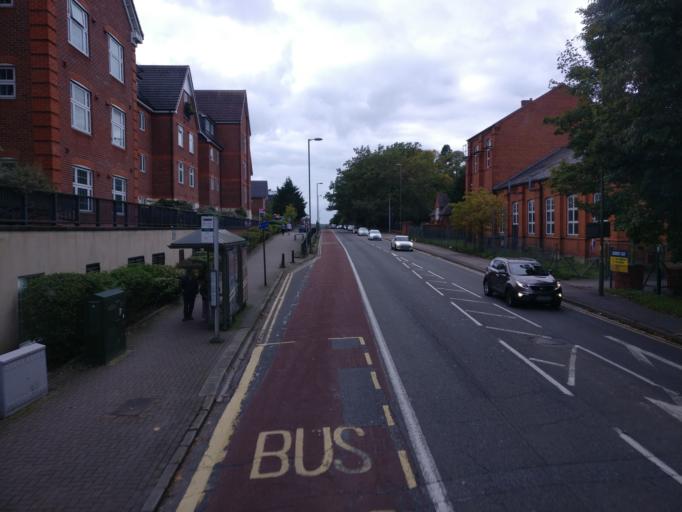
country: GB
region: England
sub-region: Surrey
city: Camberley
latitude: 51.3374
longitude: -0.7551
